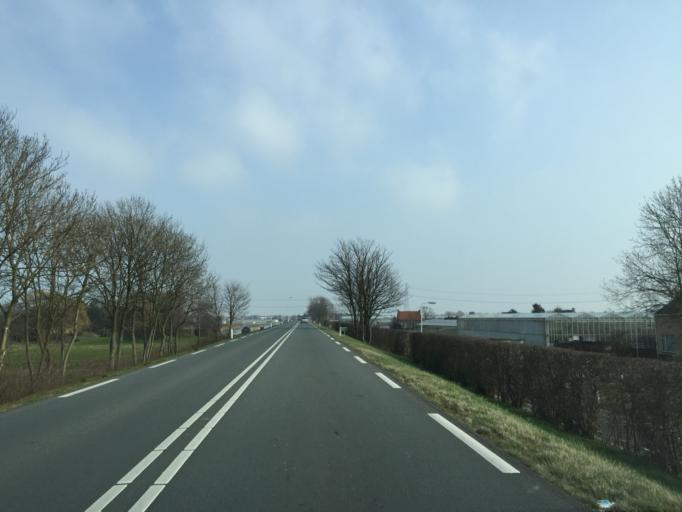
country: NL
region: South Holland
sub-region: Gemeente Westland
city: Naaldwijk
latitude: 51.9762
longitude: 4.1901
